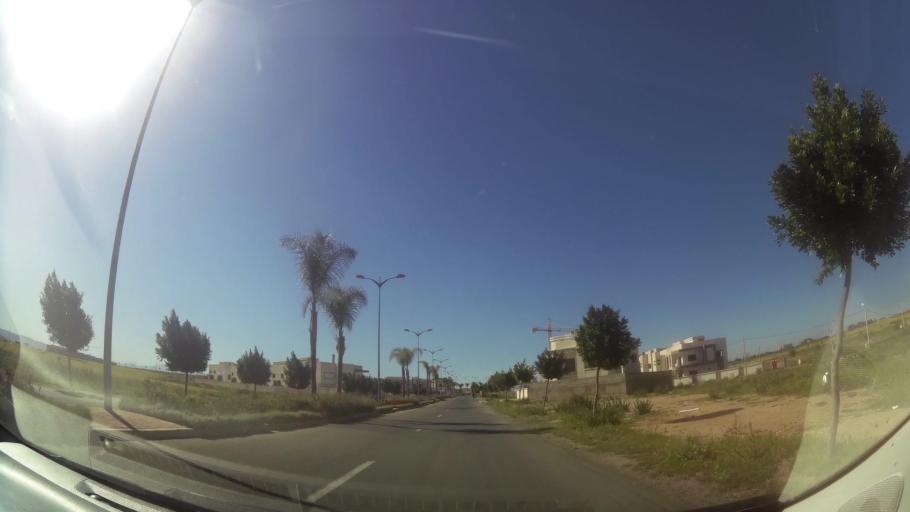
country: MA
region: Oriental
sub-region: Oujda-Angad
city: Oujda
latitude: 34.7320
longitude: -1.9175
